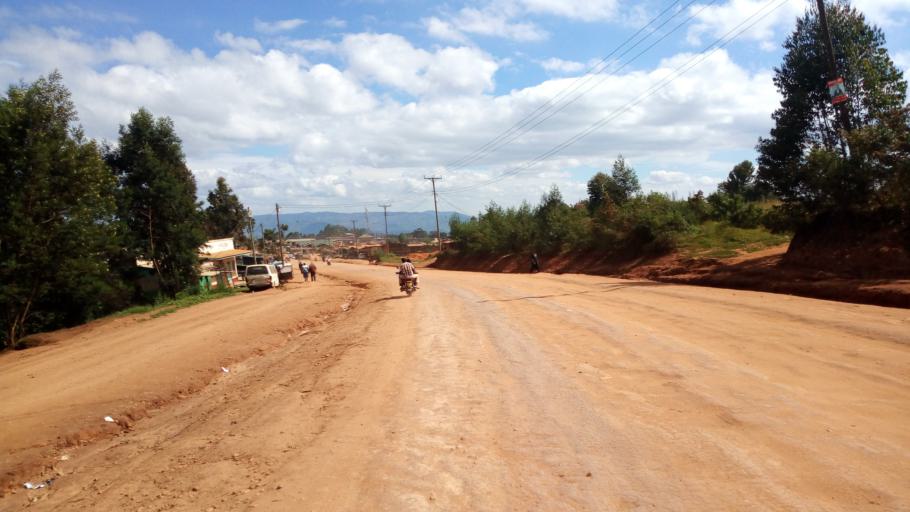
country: KE
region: Makueni
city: Wote
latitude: -1.6587
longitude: 37.4492
